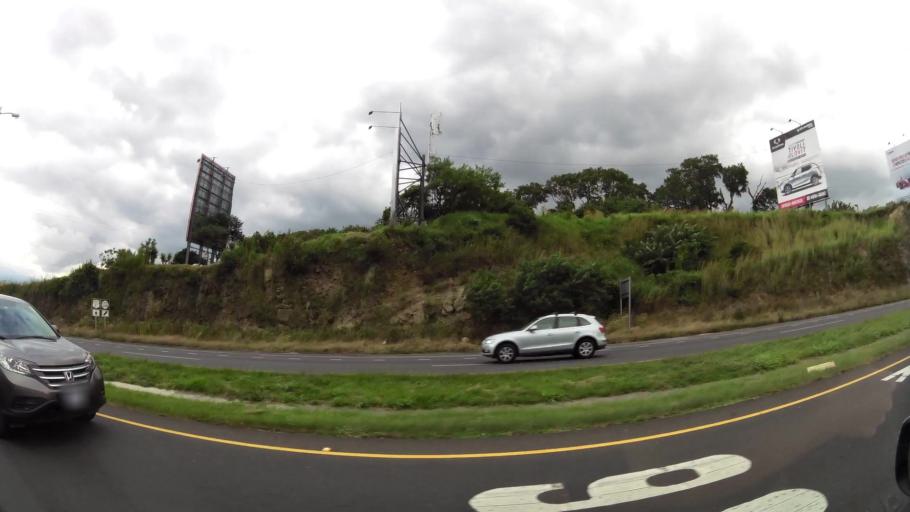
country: CR
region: San Jose
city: Santa Ana
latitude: 9.9456
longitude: -84.1650
